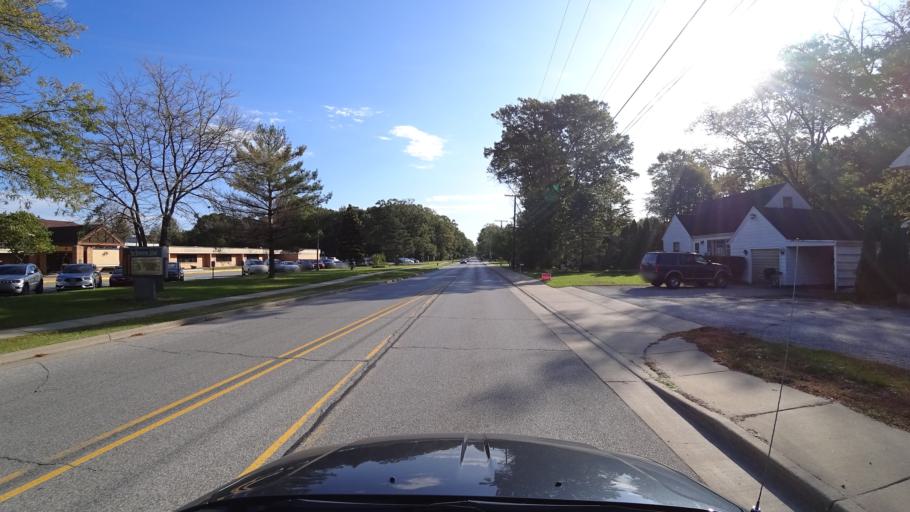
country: US
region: Indiana
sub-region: LaPorte County
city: Trail Creek
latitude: 41.6947
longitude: -86.8730
